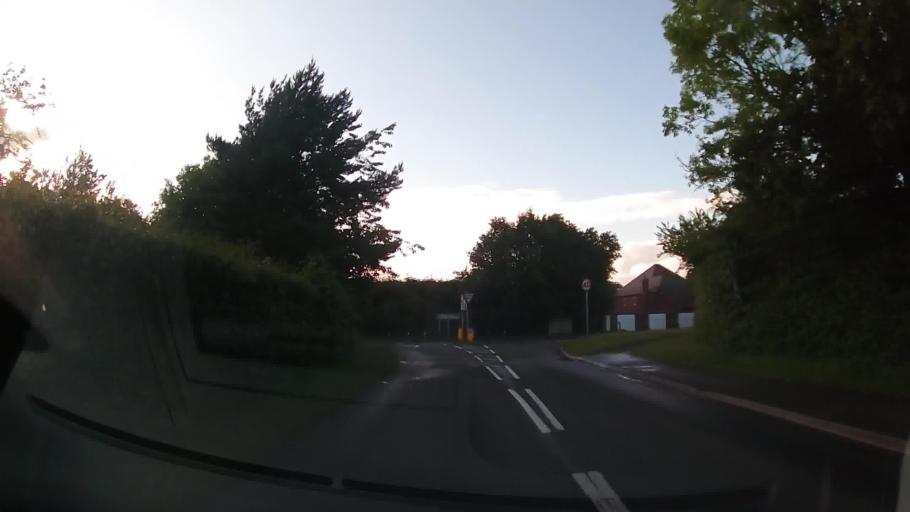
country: GB
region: England
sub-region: Leicestershire
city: Markfield
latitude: 52.6761
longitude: -1.2752
